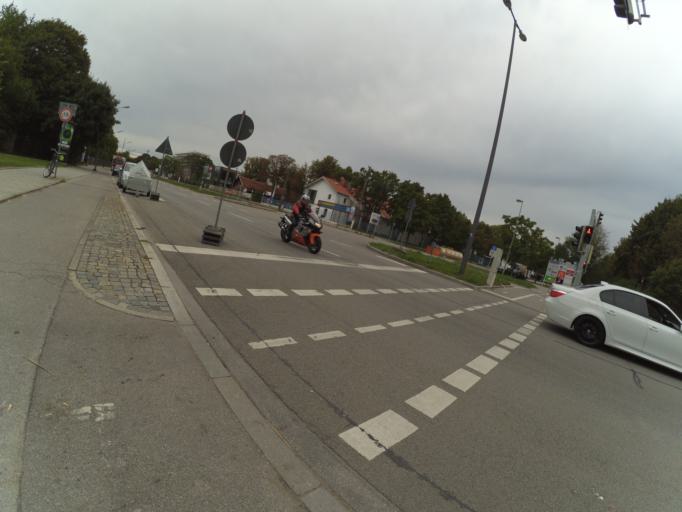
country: DE
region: Bavaria
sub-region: Upper Bavaria
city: Oberschleissheim
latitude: 48.2014
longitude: 11.5644
